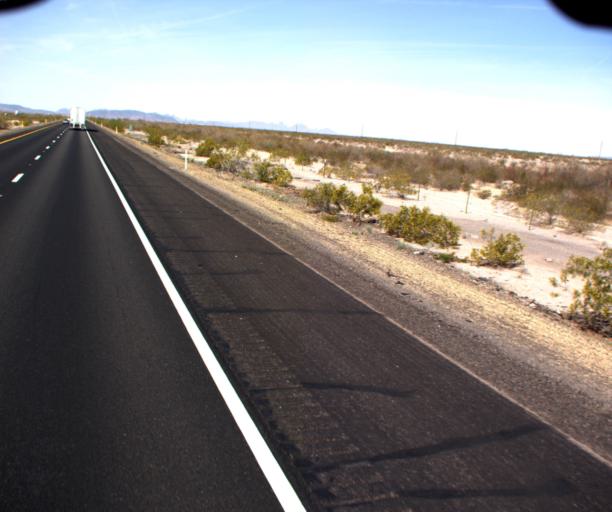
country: US
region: Arizona
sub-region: La Paz County
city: Salome
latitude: 33.6219
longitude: -113.7038
